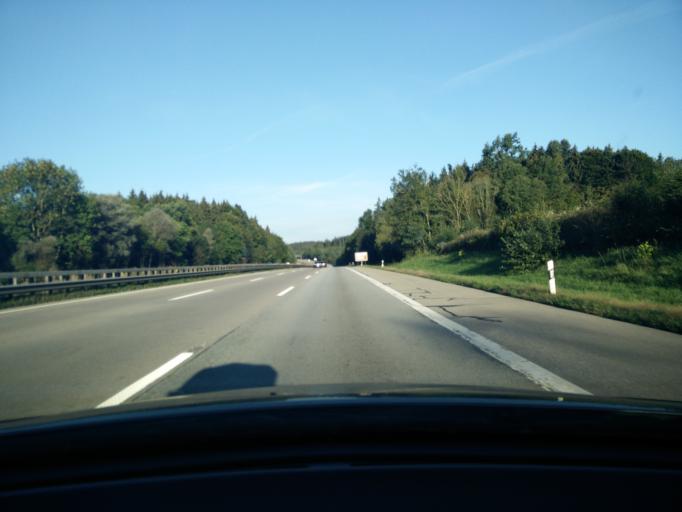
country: DE
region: Bavaria
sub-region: Upper Bavaria
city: Weyarn
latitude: 47.8626
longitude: 11.8377
